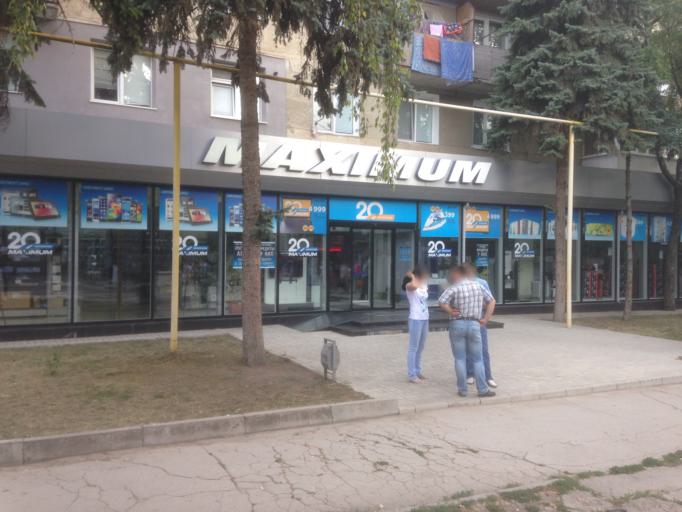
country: MD
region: Balti
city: Balti
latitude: 47.7618
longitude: 27.9262
